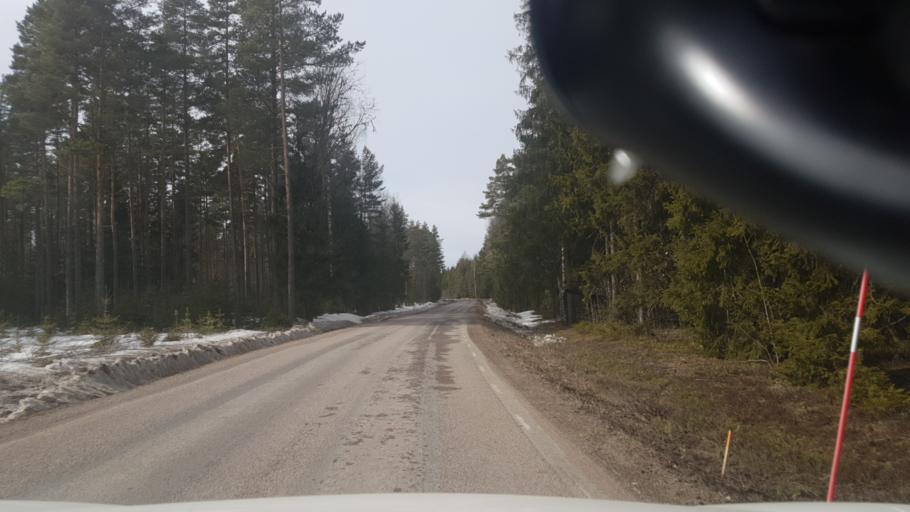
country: SE
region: Vaermland
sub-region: Eda Kommun
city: Charlottenberg
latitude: 59.8519
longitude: 12.3255
